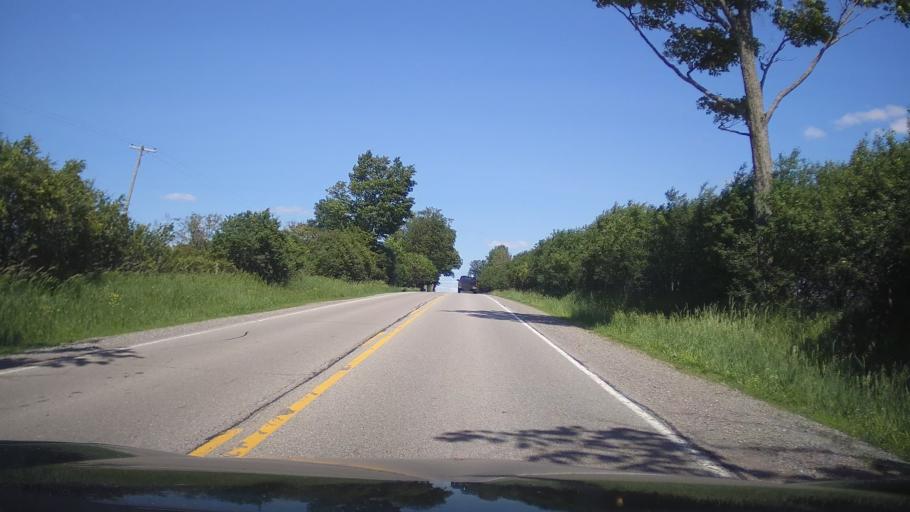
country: CA
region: Ontario
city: Oshawa
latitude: 44.0051
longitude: -78.8134
